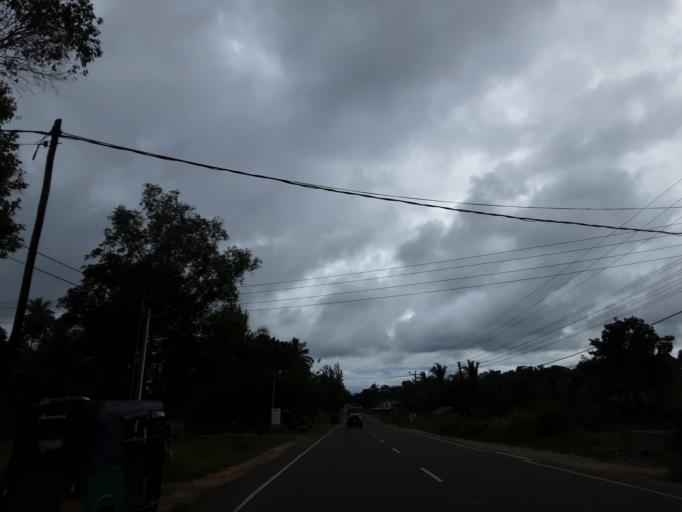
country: LK
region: Uva
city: Badulla
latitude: 7.3754
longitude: 81.0678
